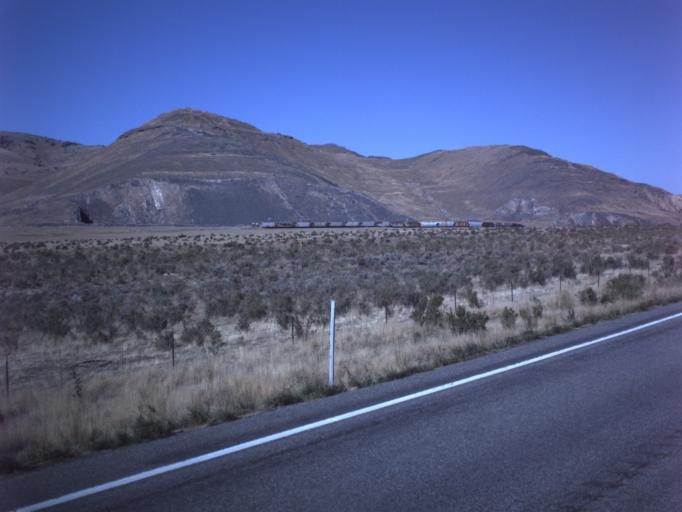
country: US
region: Utah
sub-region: Tooele County
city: Grantsville
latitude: 40.6677
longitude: -112.5445
